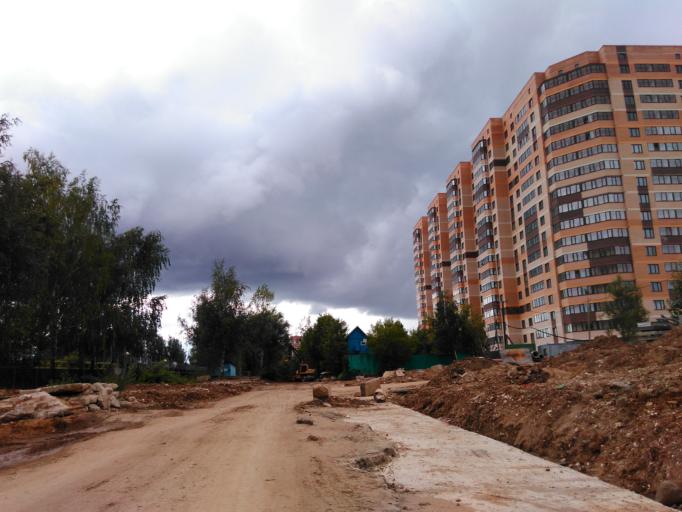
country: RU
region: Moscow
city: Ramenki
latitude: 55.6857
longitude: 37.5119
